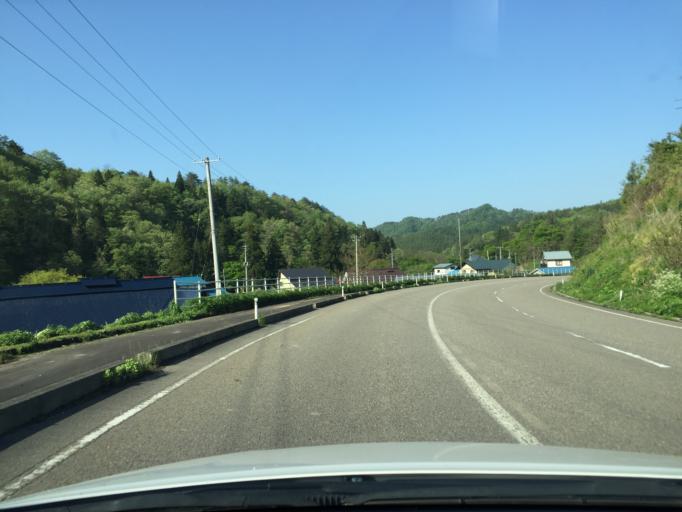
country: JP
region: Fukushima
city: Kitakata
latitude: 37.6683
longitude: 139.8121
